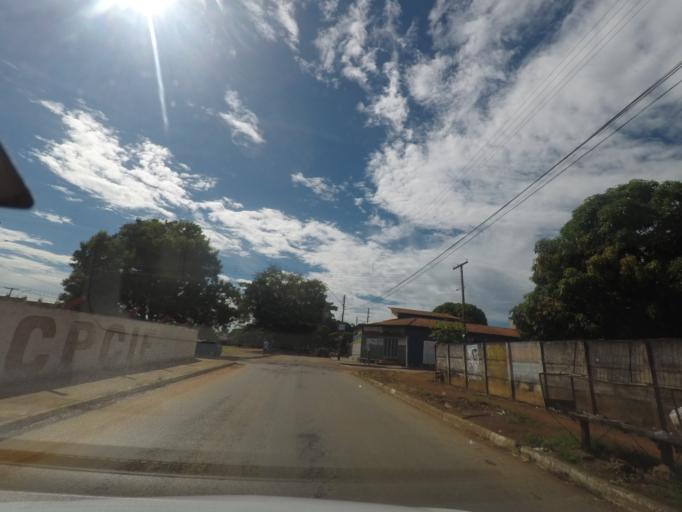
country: BR
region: Goias
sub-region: Aparecida De Goiania
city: Aparecida de Goiania
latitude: -16.7967
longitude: -49.2788
